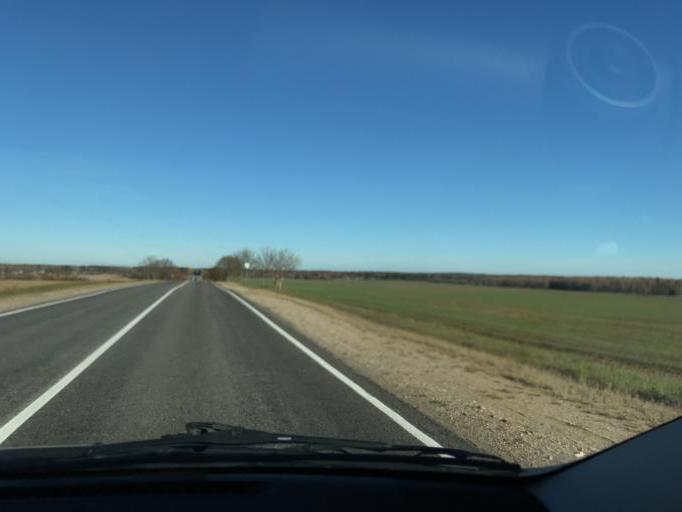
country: BY
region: Vitebsk
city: Lyepyel'
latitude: 55.0416
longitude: 28.7492
